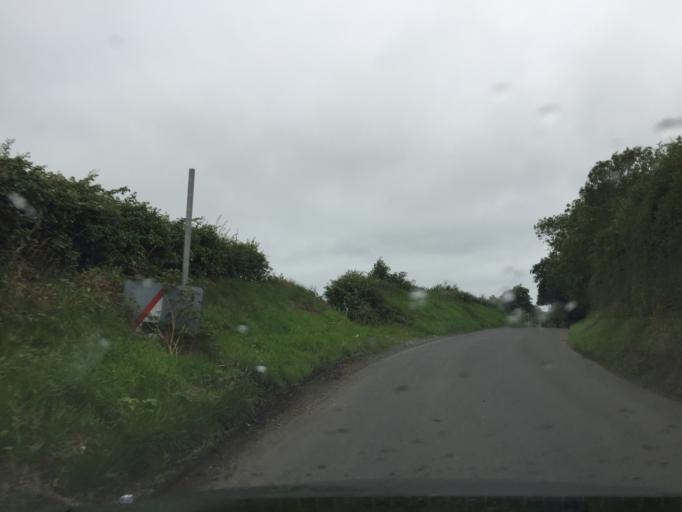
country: GB
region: Northern Ireland
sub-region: Down District
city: Kircubbin
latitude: 54.4902
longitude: -5.5164
